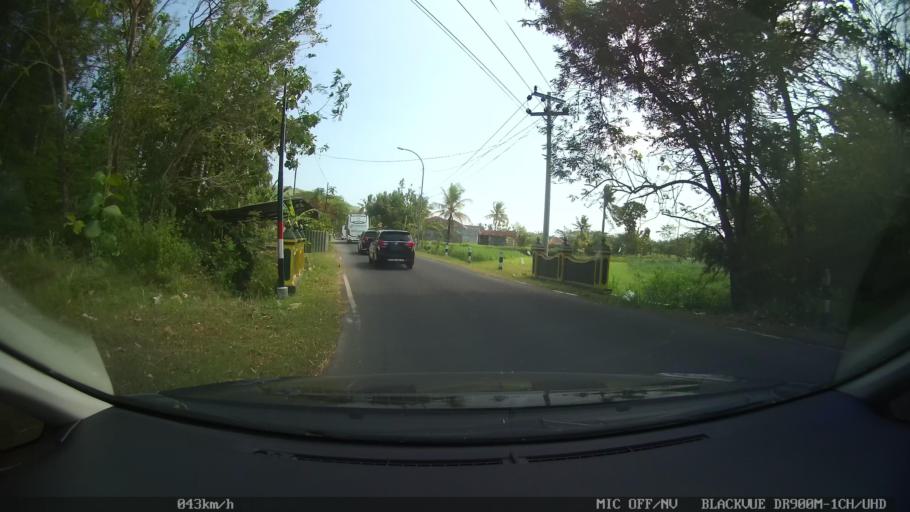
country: ID
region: Daerah Istimewa Yogyakarta
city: Pundong
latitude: -7.9773
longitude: 110.3409
